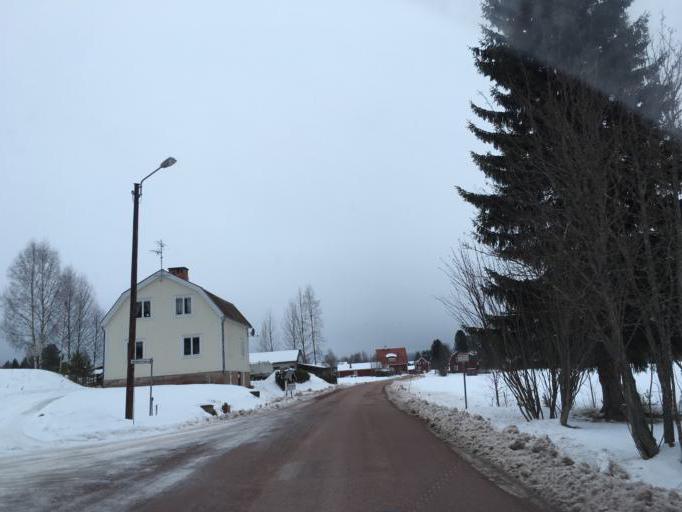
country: SE
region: Dalarna
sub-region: Alvdalens Kommun
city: AElvdalen
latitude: 61.2575
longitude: 14.0508
